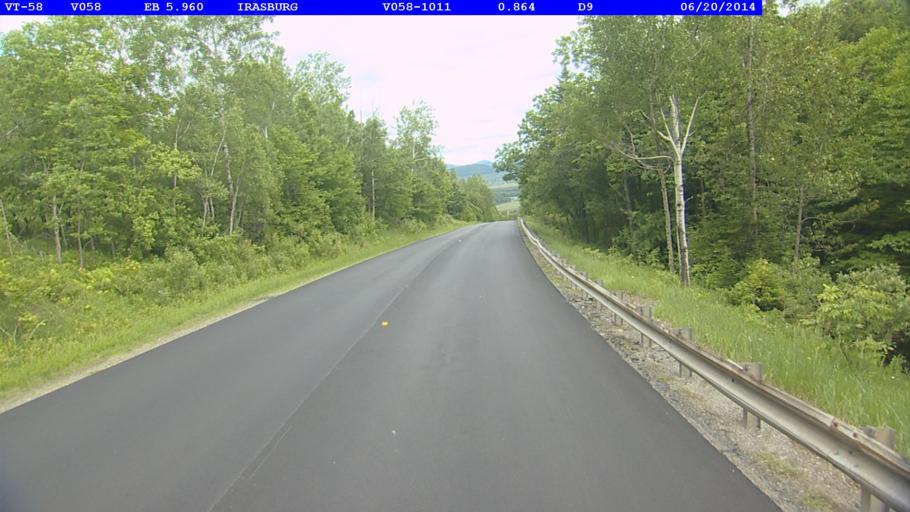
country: US
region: Vermont
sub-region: Orleans County
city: Newport
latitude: 44.8185
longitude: -72.3416
